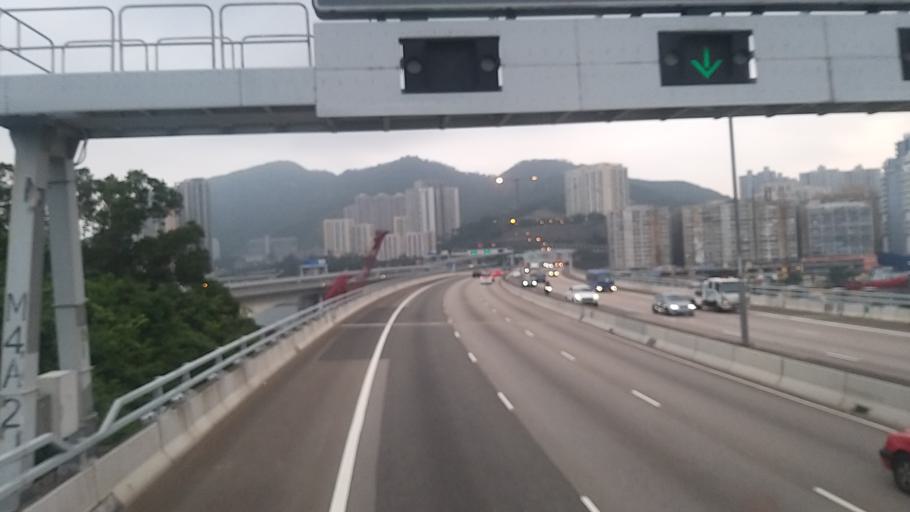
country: HK
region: Tsuen Wan
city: Tsuen Wan
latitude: 22.3507
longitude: 114.1165
